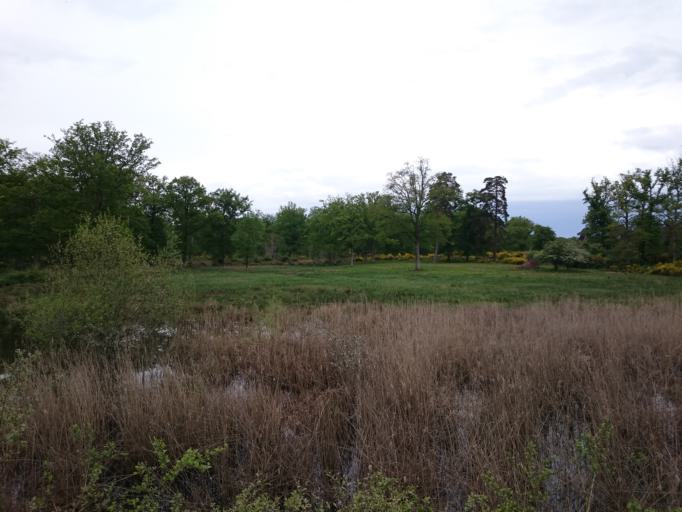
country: FR
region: Centre
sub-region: Departement du Loir-et-Cher
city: Muides-sur-Loire
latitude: 47.6186
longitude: 1.5300
